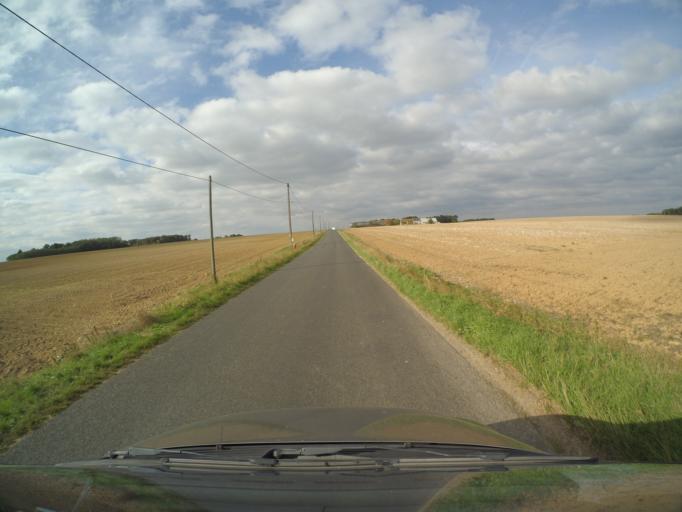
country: FR
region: Centre
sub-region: Departement d'Indre-et-Loire
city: Nazelles-Negron
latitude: 47.4739
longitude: 0.9536
